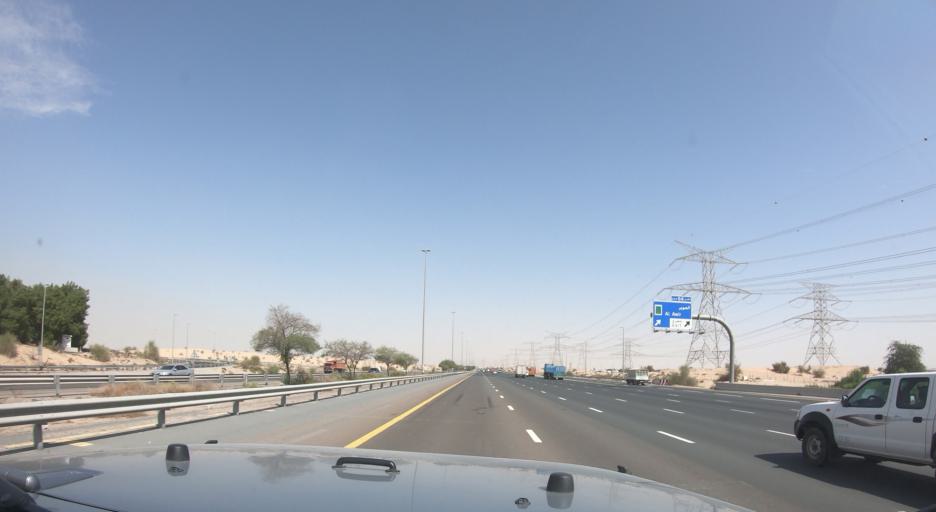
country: AE
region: Ash Shariqah
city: Sharjah
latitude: 25.1891
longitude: 55.5297
